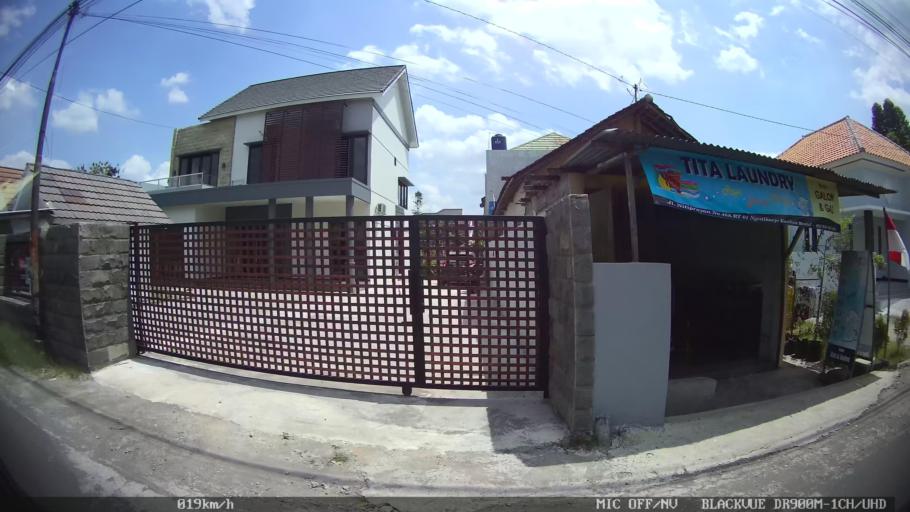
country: ID
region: Daerah Istimewa Yogyakarta
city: Kasihan
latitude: -7.8127
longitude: 110.3433
